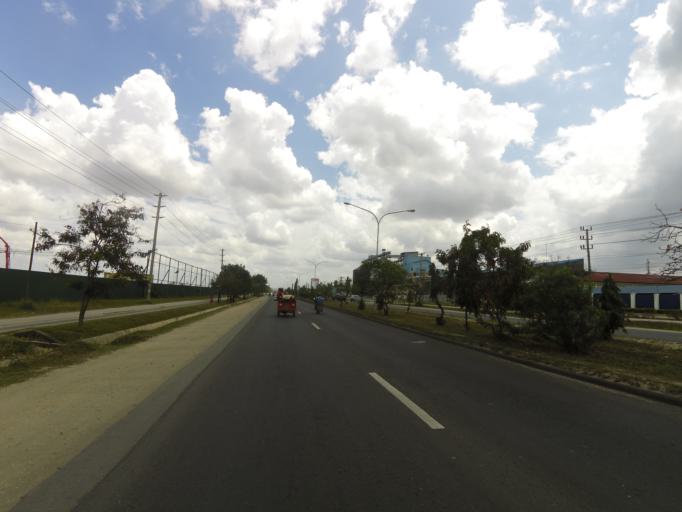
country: TZ
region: Dar es Salaam
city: Dar es Salaam
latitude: -6.8603
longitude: 39.2124
